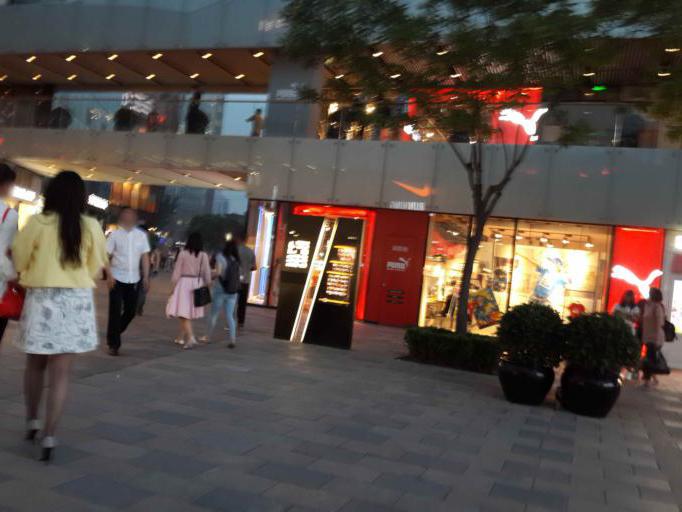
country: CN
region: Beijing
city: Chaowai
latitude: 39.9334
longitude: 116.4482
